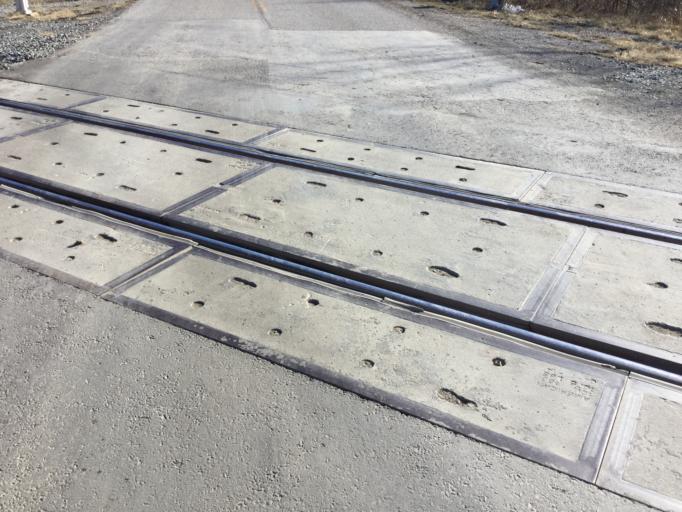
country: US
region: Kansas
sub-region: Miami County
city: Osawatomie
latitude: 38.3312
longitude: -94.9856
